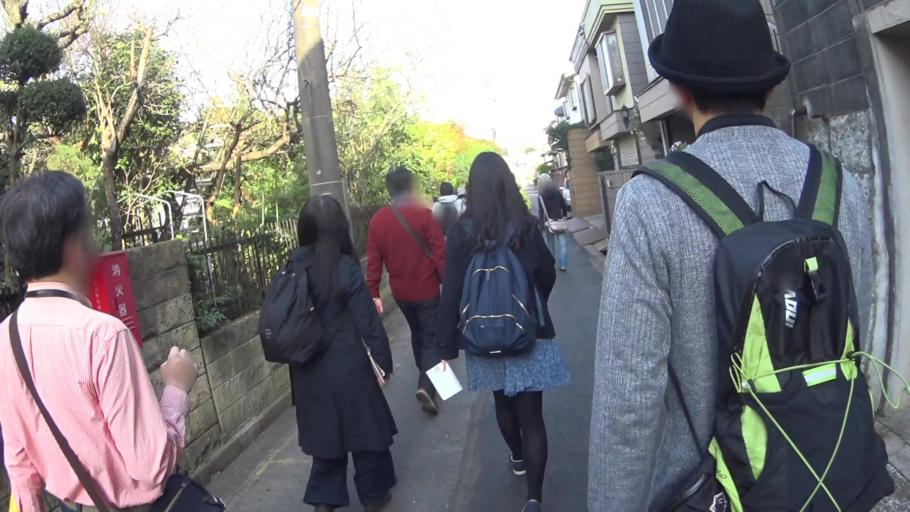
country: JP
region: Tokyo
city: Kokubunji
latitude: 35.7185
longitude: 139.4987
